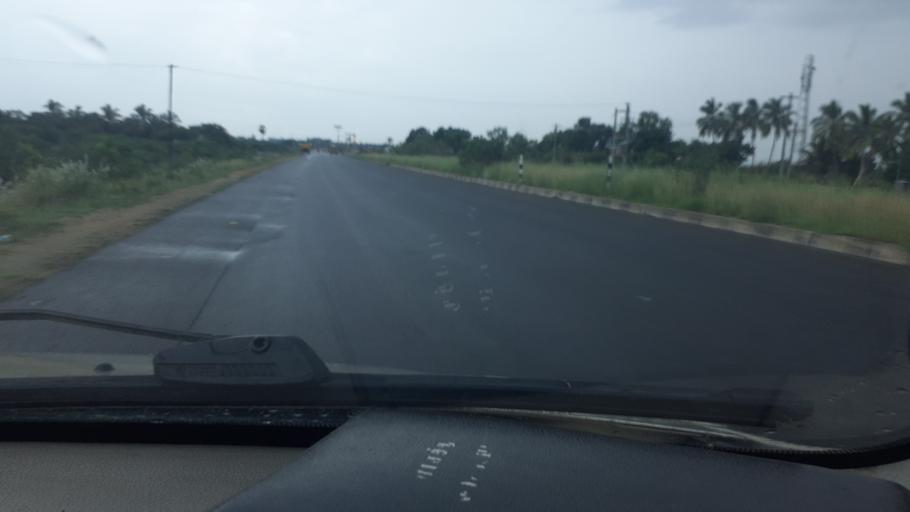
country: IN
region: Tamil Nadu
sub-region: Thoothukkudi
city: Kadambur
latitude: 9.0501
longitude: 77.7953
